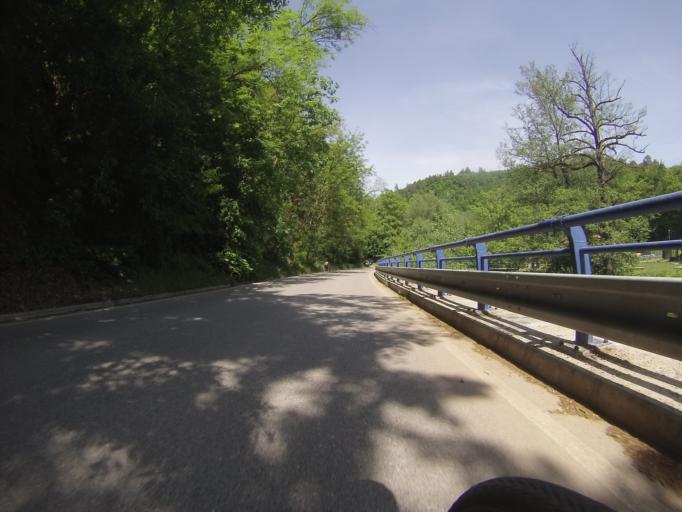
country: CZ
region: South Moravian
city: Bilovice nad Svitavou
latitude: 49.2775
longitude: 16.6723
